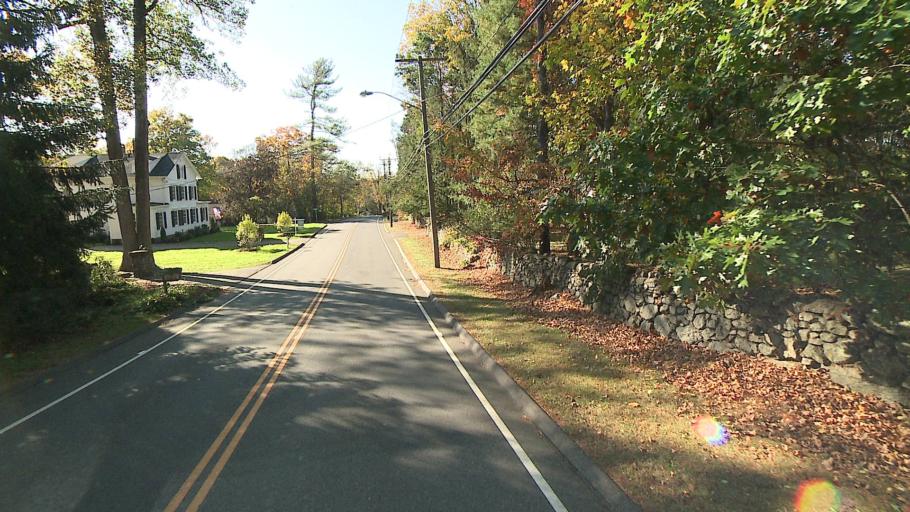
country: US
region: Connecticut
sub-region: Fairfield County
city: Westport
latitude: 41.1624
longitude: -73.3936
